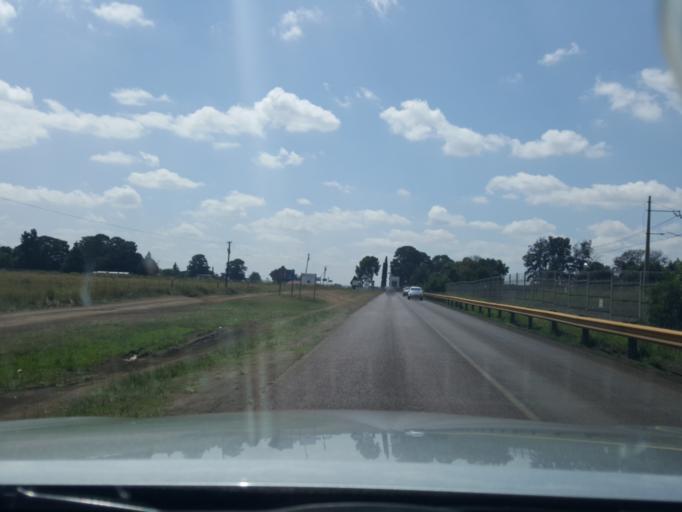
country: ZA
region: Mpumalanga
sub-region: Nkangala District Municipality
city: Middelburg
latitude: -25.9737
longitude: 29.4502
